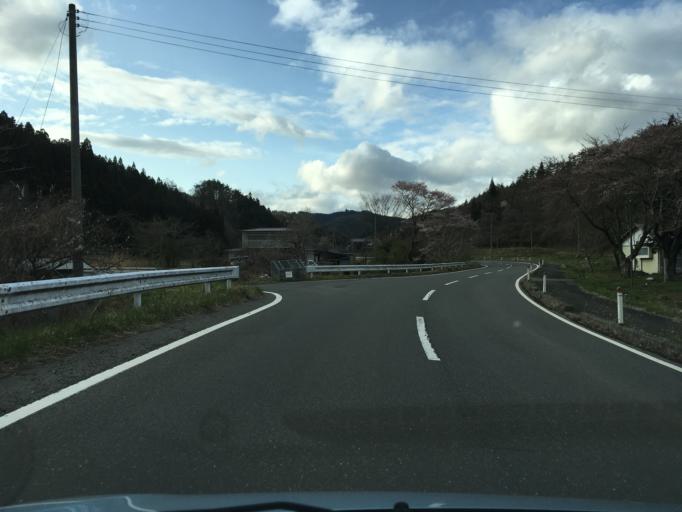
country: JP
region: Iwate
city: Ichinoseki
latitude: 38.7945
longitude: 141.3204
